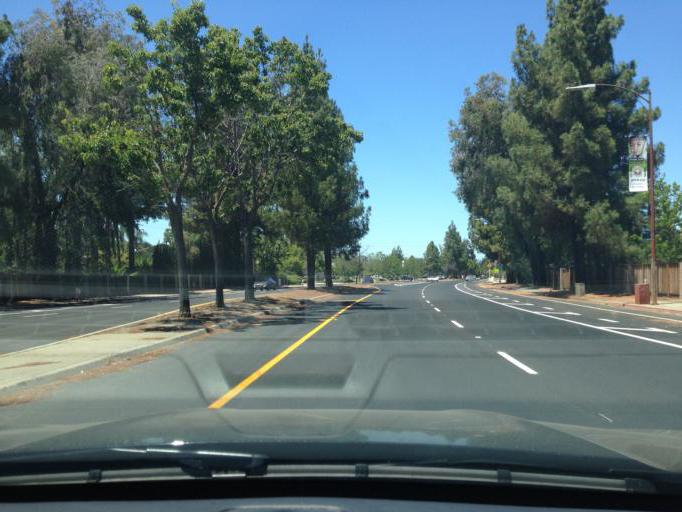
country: US
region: California
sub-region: Santa Clara County
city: Seven Trees
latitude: 37.2209
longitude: -121.8658
